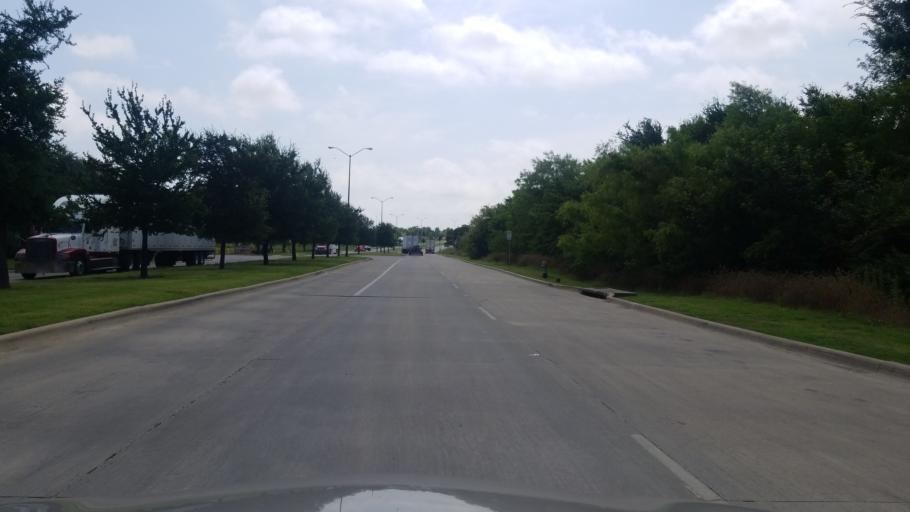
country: US
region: Texas
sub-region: Dallas County
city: Duncanville
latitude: 32.6896
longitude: -96.9612
